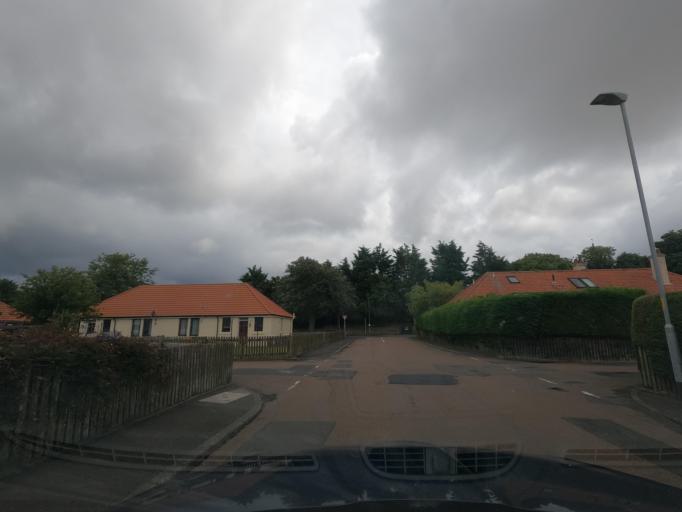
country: GB
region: England
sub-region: Northumberland
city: Ancroft
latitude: 55.7373
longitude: -1.9925
